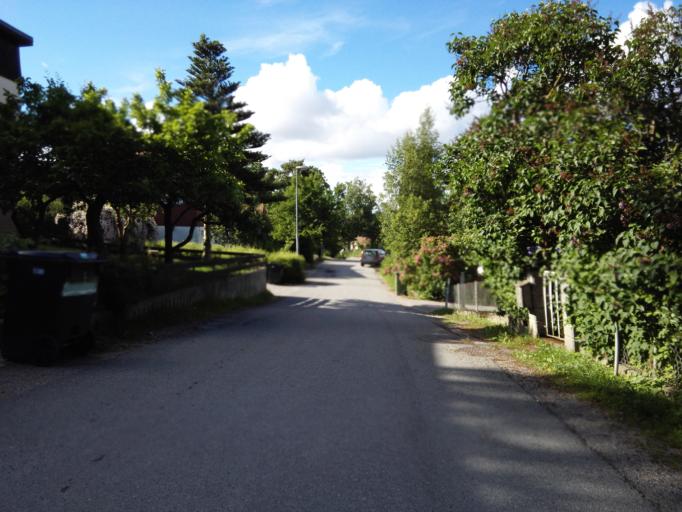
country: SE
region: Stockholm
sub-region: Huddinge Kommun
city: Huddinge
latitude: 59.2634
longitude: 17.9721
